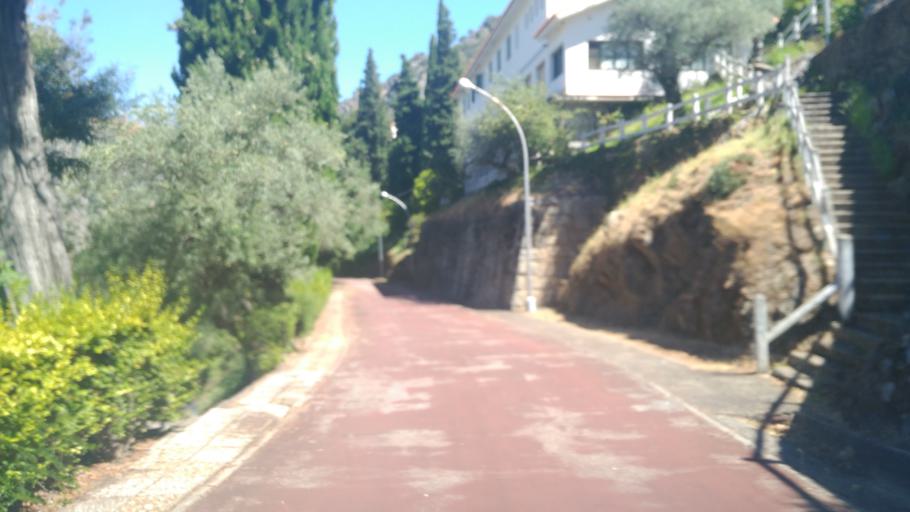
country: ES
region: Castille and Leon
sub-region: Provincia de Salamanca
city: Mieza
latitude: 41.1920
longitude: -6.6898
